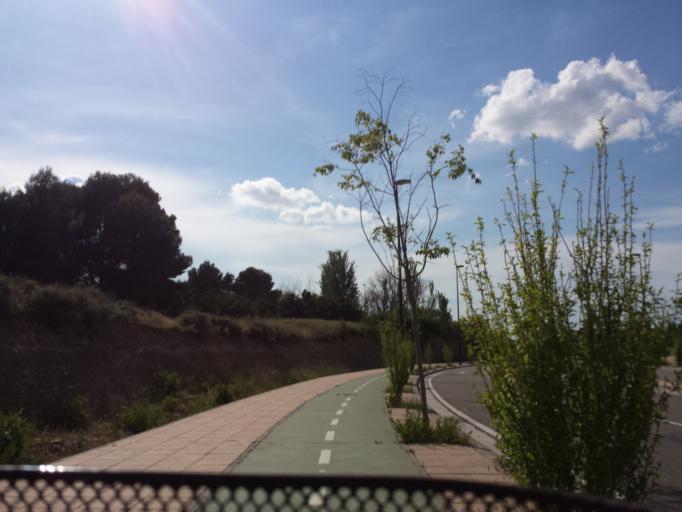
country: ES
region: Aragon
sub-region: Provincia de Zaragoza
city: Montecanal
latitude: 41.6342
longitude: -0.9371
